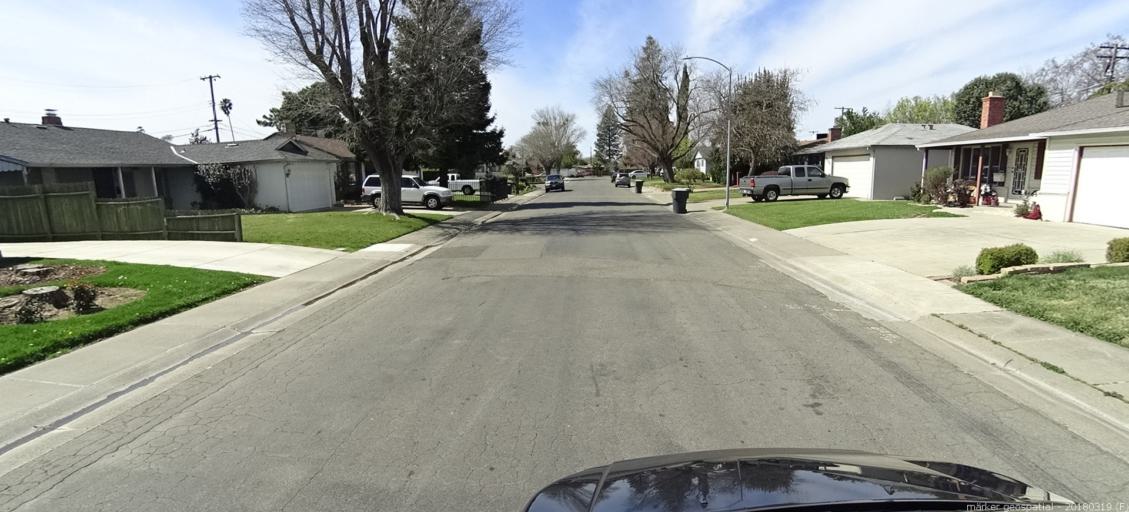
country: US
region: California
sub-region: Sacramento County
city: Parkway
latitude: 38.5151
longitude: -121.4491
